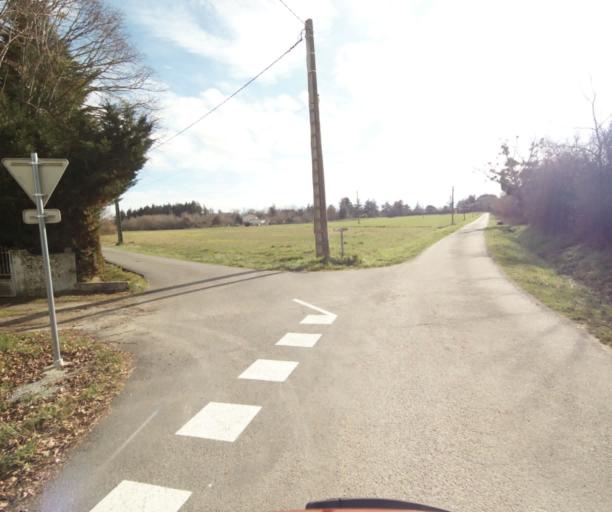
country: FR
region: Midi-Pyrenees
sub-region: Departement de l'Ariege
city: La Tour-du-Crieu
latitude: 43.1329
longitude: 1.6990
